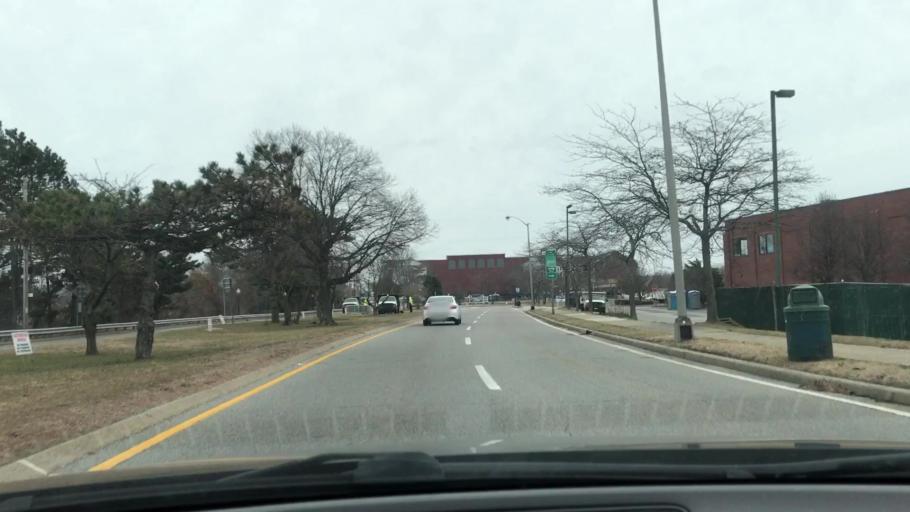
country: US
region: New York
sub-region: Suffolk County
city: Patchogue
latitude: 40.7673
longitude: -73.0218
